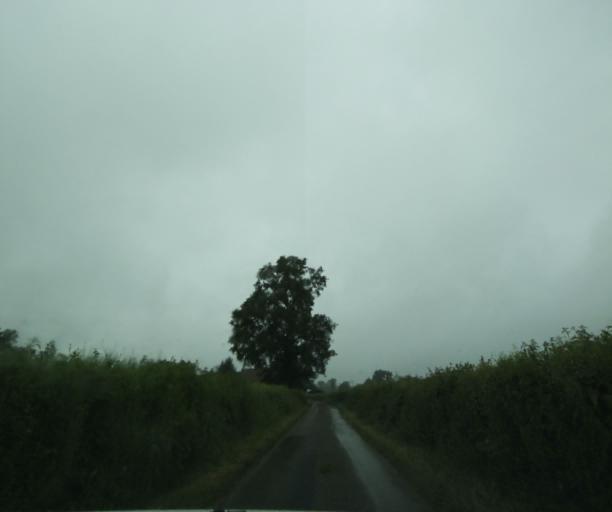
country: FR
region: Bourgogne
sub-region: Departement de Saone-et-Loire
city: Charolles
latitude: 46.3996
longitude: 4.2379
